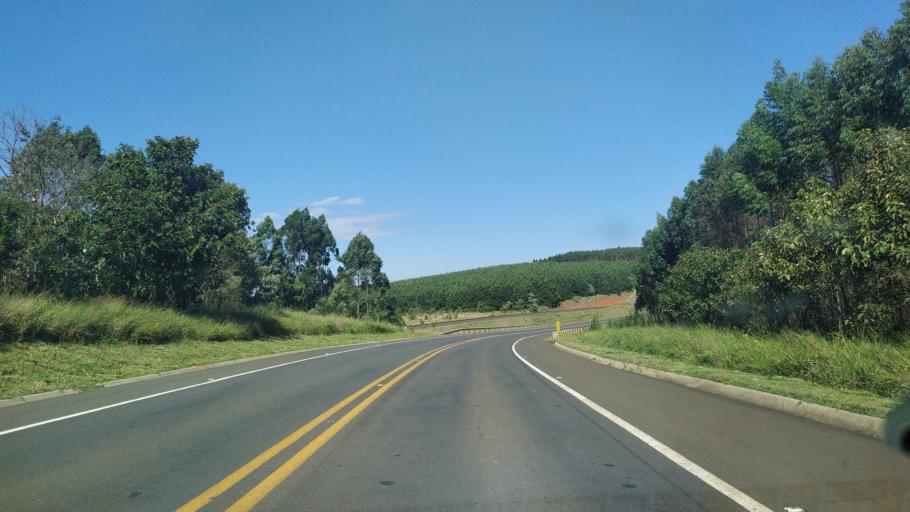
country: BR
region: Parana
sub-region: Telemaco Borba
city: Telemaco Borba
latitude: -24.2521
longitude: -50.7769
